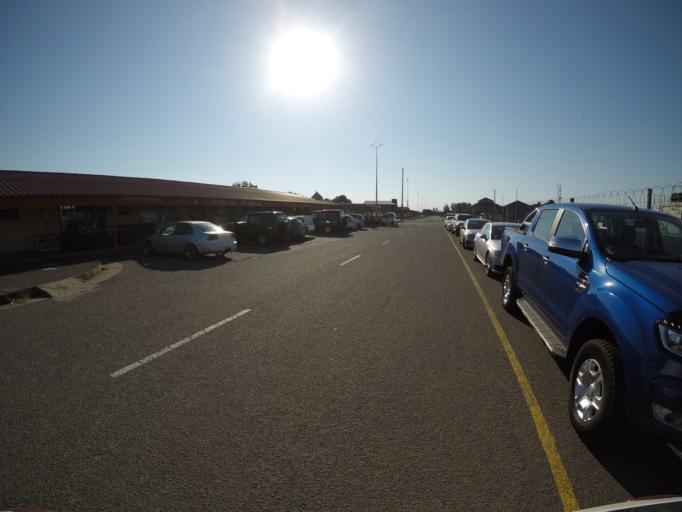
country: ZA
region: KwaZulu-Natal
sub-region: uThungulu District Municipality
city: Richards Bay
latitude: -28.7961
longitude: 32.0784
